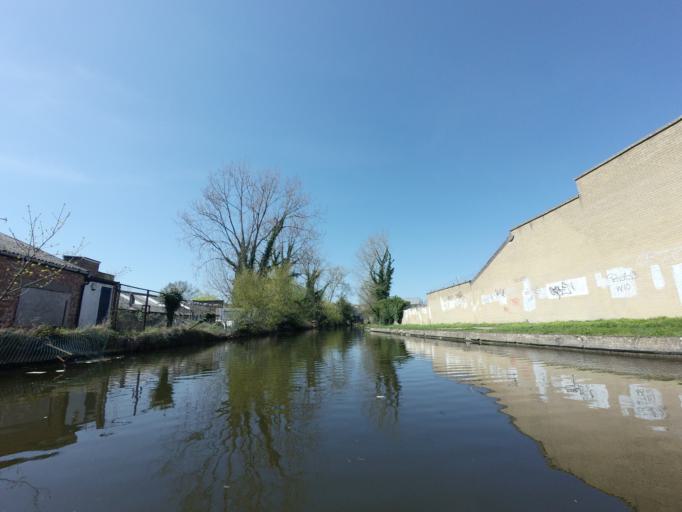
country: GB
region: England
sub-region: Greater London
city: West Drayton
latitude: 51.5125
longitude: -0.4755
